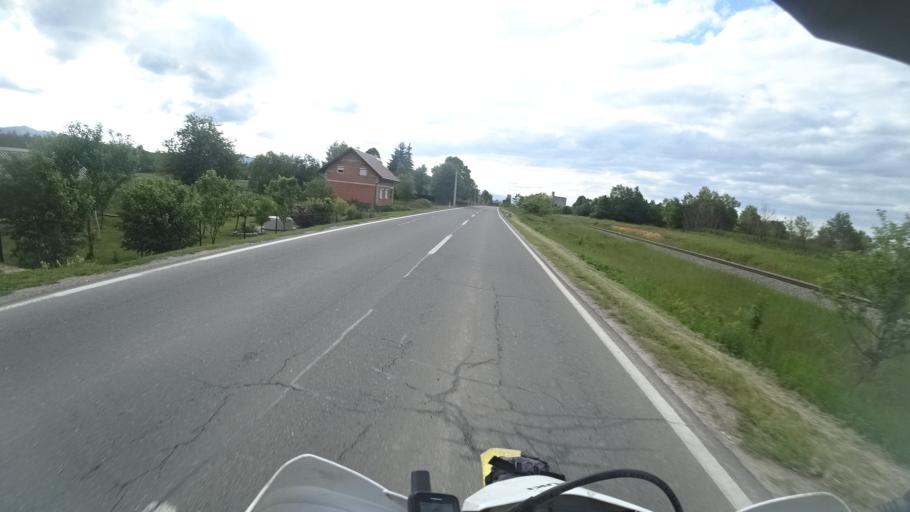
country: HR
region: Licko-Senjska
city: Gospic
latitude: 44.5285
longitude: 15.4060
